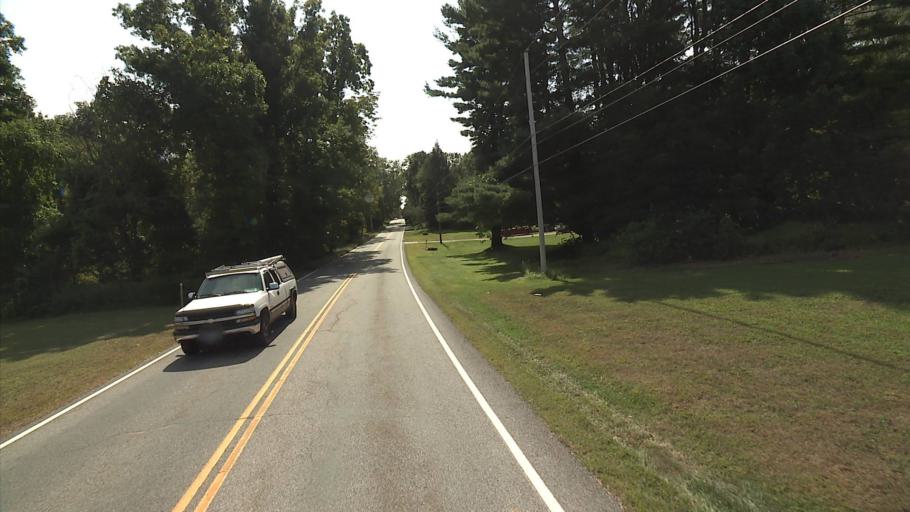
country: US
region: Connecticut
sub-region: Windham County
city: Plainfield Village
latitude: 41.7099
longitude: -71.9695
